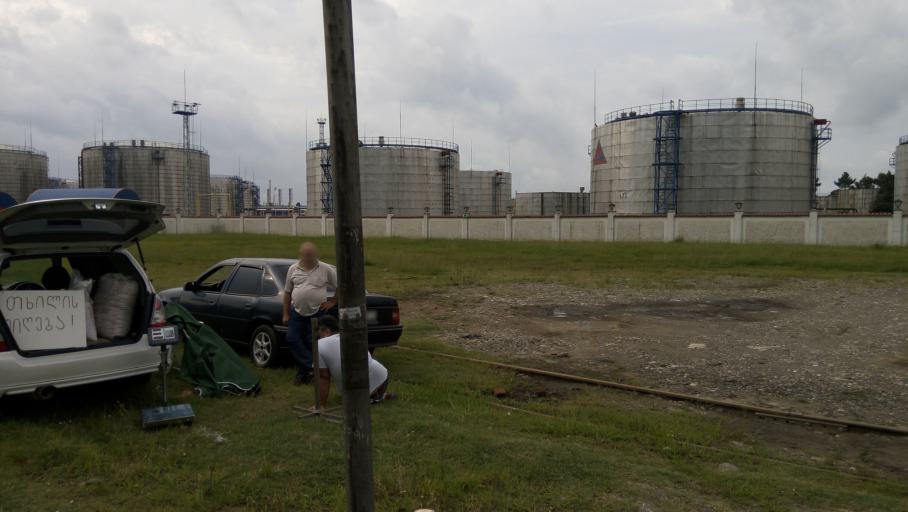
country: GE
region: Ajaria
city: Batumi
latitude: 41.6417
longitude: 41.6638
